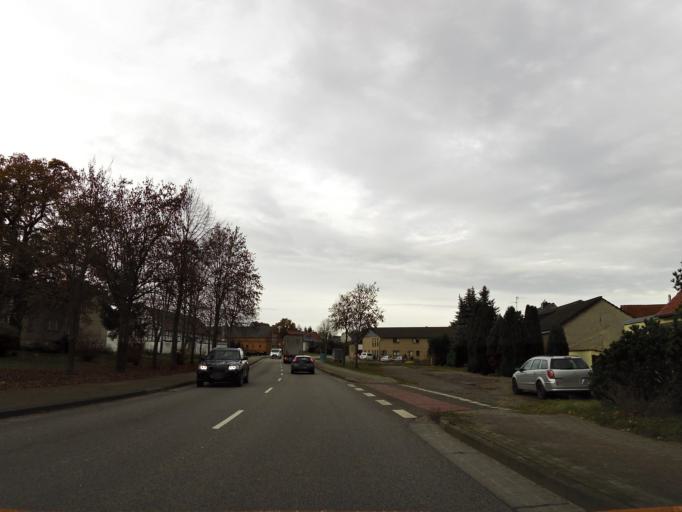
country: DE
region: Saxony-Anhalt
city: Kalbe
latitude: 52.6612
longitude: 11.2824
